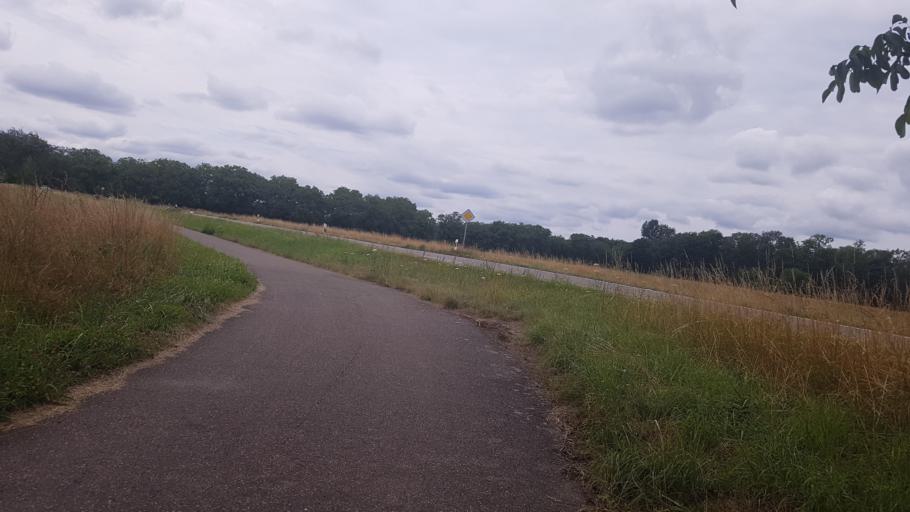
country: DE
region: Baden-Wuerttemberg
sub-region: Karlsruhe Region
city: Rheinau
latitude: 48.8822
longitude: 8.2059
